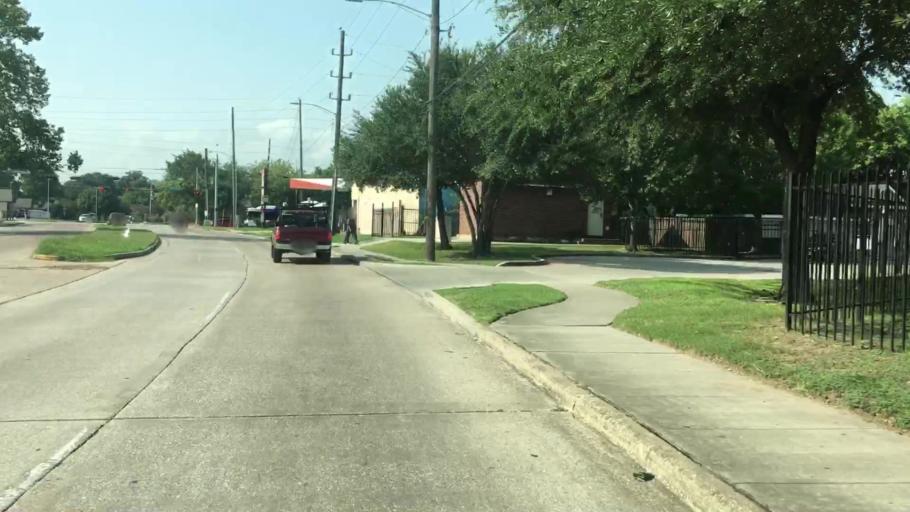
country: US
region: Texas
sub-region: Harris County
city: Aldine
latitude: 29.9330
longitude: -95.4022
